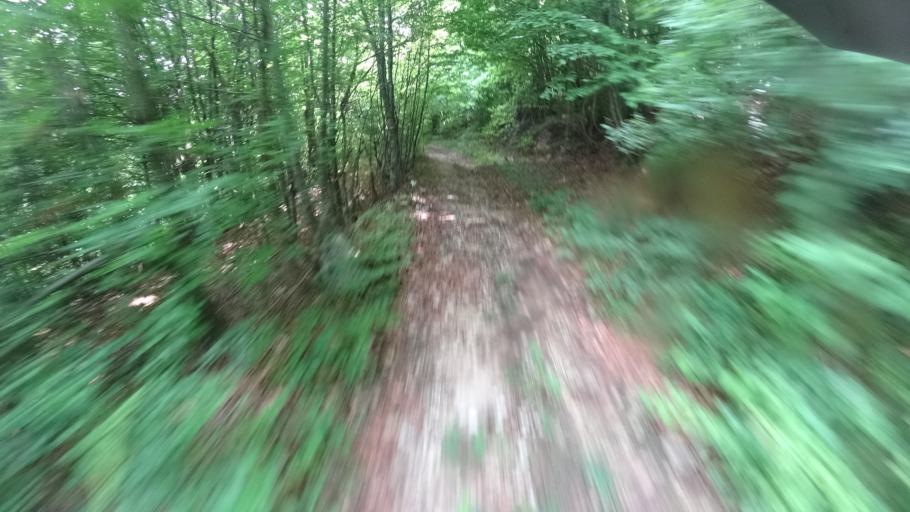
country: HR
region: Licko-Senjska
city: Jezerce
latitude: 44.8781
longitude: 15.7009
